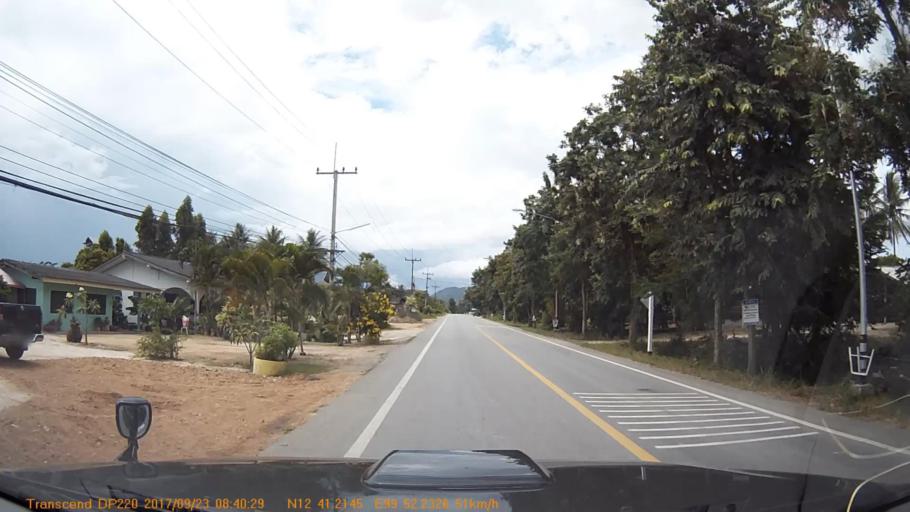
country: TH
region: Prachuap Khiri Khan
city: Hua Hin
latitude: 12.6870
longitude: 99.8705
